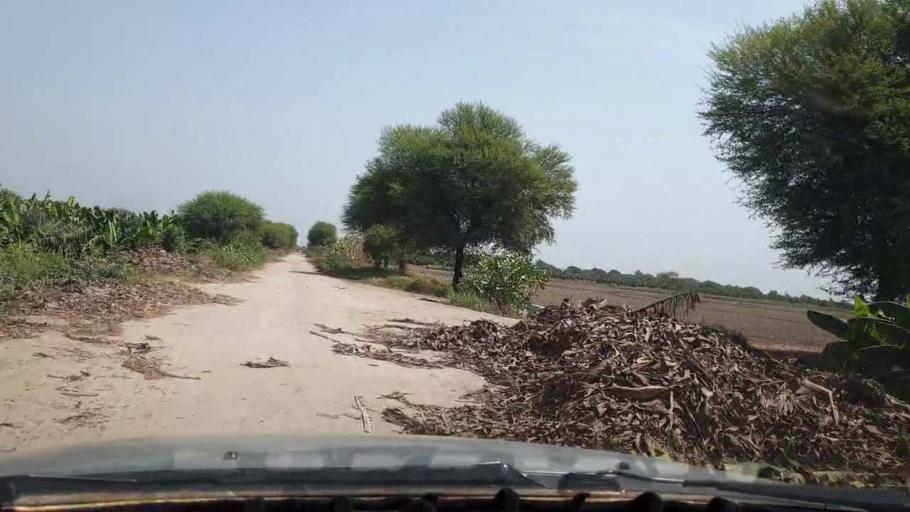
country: PK
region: Sindh
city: Tando Muhammad Khan
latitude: 25.1754
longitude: 68.6416
